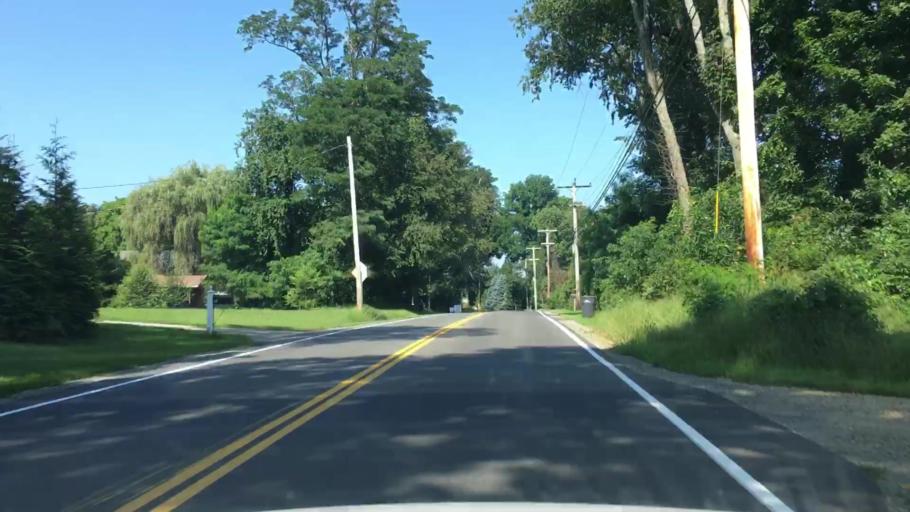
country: US
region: New Hampshire
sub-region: Rockingham County
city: East Kingston
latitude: 42.9219
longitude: -70.9959
